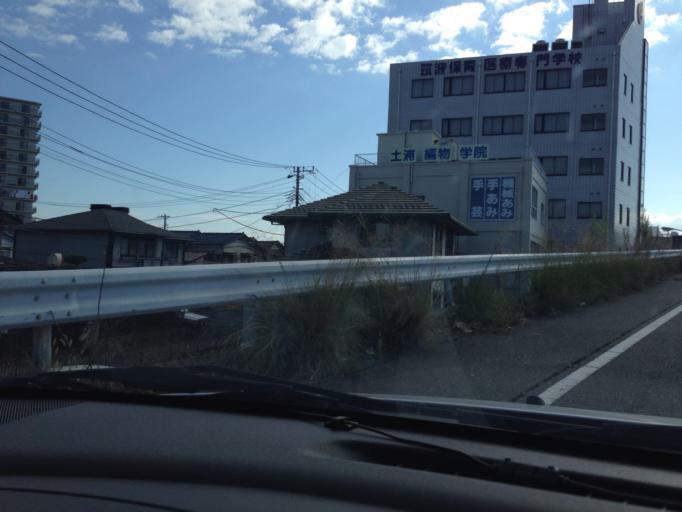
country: JP
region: Ibaraki
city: Ami
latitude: 36.0838
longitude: 140.2066
